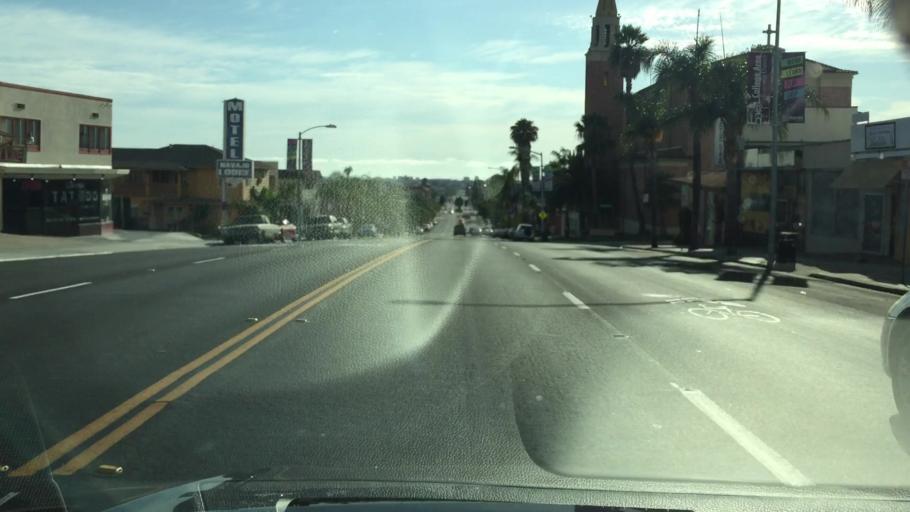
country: US
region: California
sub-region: San Diego County
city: Lemon Grove
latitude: 32.7588
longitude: -117.0730
